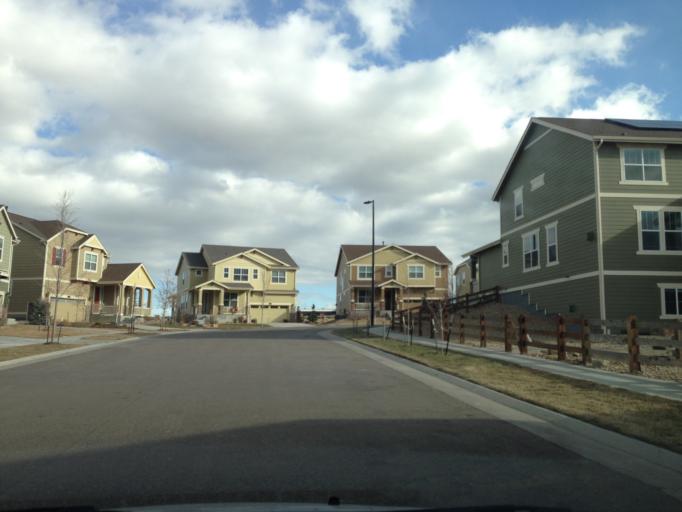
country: US
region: Colorado
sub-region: Boulder County
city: Lafayette
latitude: 40.0336
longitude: -105.0875
